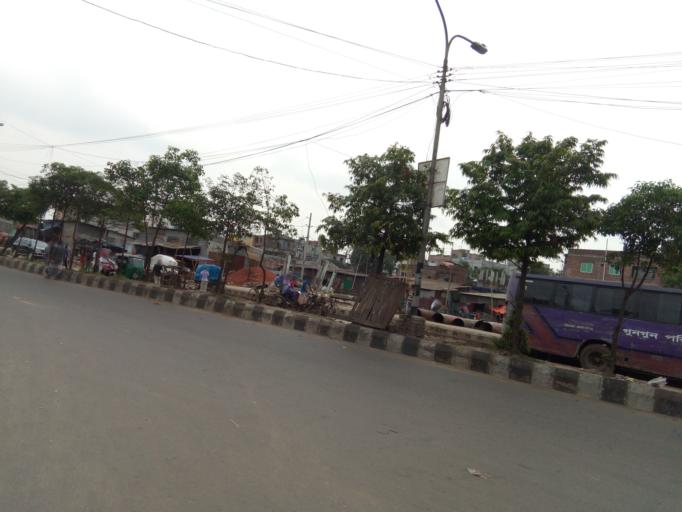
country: BD
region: Dhaka
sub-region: Dhaka
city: Dhaka
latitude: 23.6977
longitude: 90.4316
